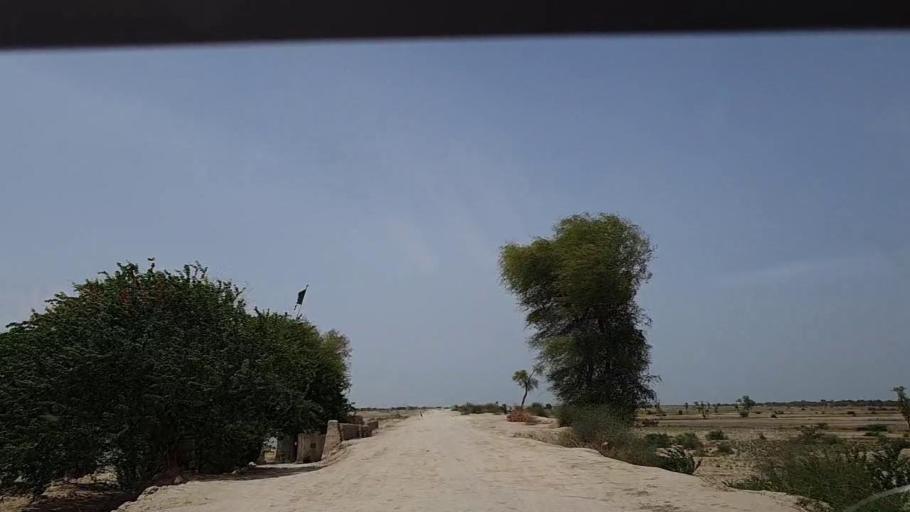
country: PK
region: Sindh
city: Johi
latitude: 26.7301
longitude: 67.6821
